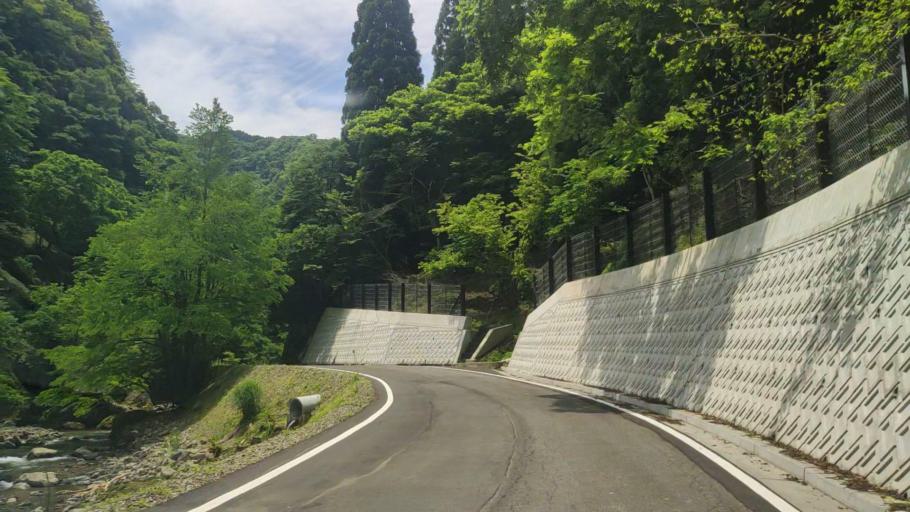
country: JP
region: Tottori
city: Tottori
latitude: 35.4091
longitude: 134.5065
